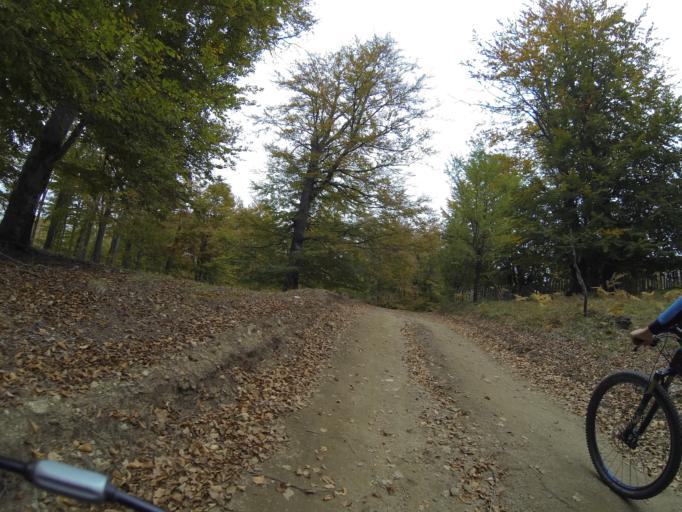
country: RO
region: Gorj
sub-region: Comuna Tismana
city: Sohodol
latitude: 45.1252
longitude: 22.8609
